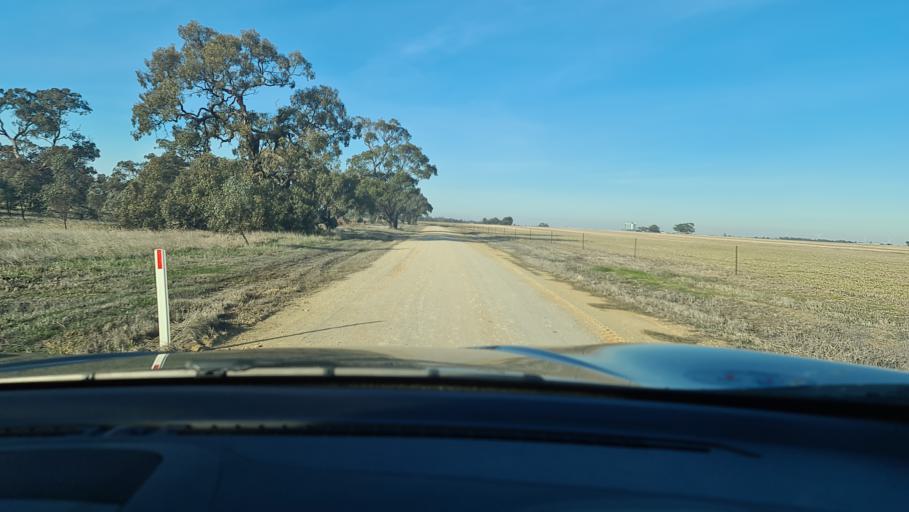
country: AU
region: Victoria
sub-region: Horsham
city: Horsham
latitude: -36.3574
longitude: 142.3964
